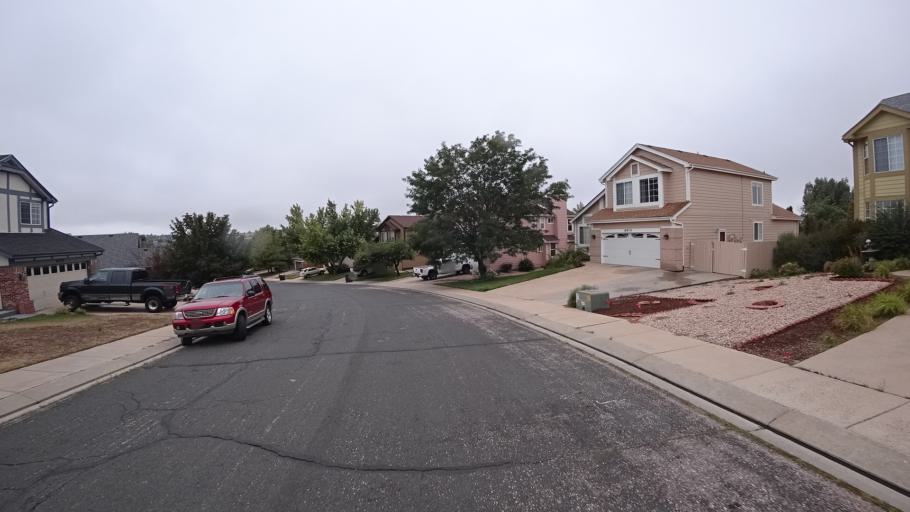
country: US
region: Colorado
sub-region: El Paso County
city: Cimarron Hills
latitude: 38.9341
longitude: -104.7536
